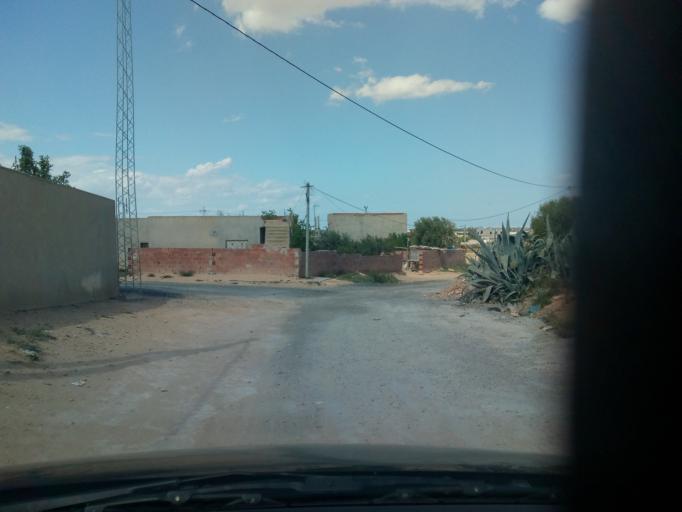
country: TN
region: Safaqis
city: Sfax
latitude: 34.7261
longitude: 10.6083
